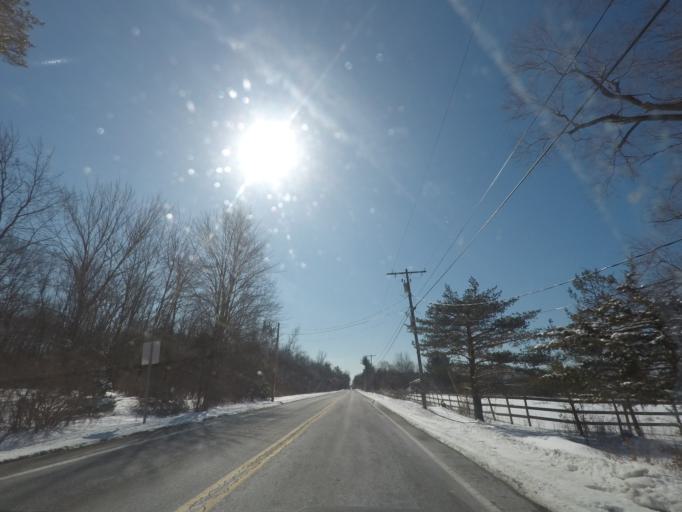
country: US
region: New York
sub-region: Saratoga County
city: Ballston Spa
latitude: 42.9829
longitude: -73.8326
